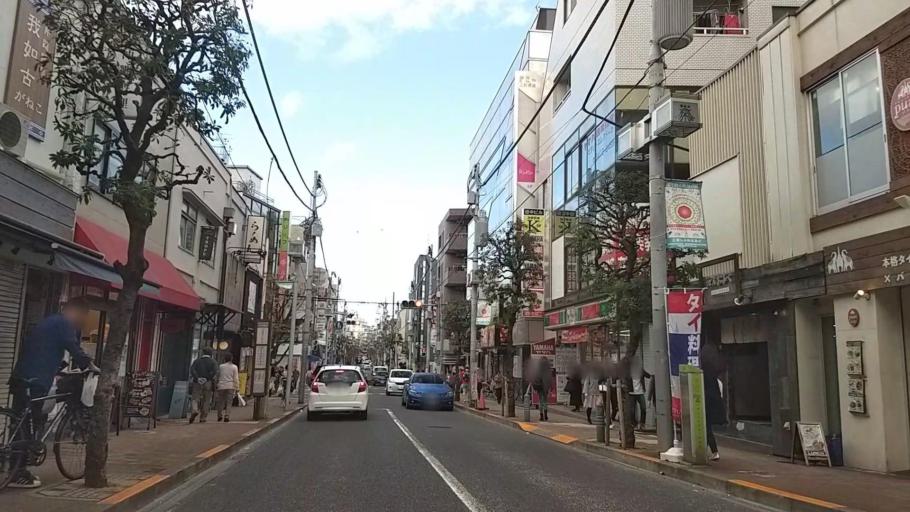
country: JP
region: Tokyo
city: Tokyo
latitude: 35.6467
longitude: 139.6696
